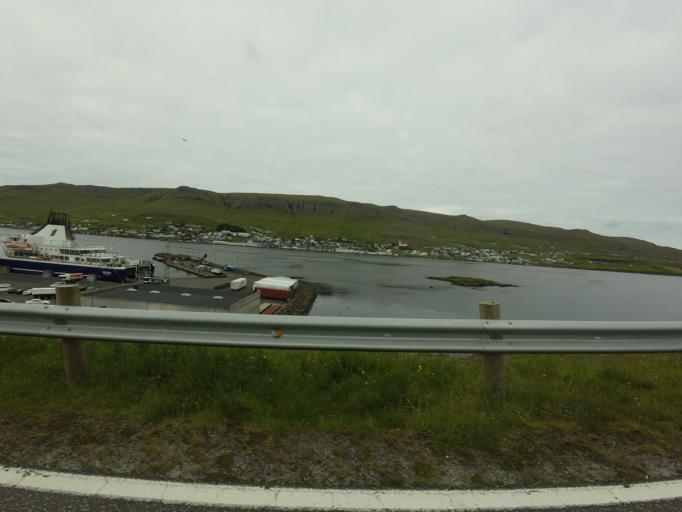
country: FO
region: Suduroy
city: Tvoroyri
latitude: 61.5470
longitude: -6.8174
